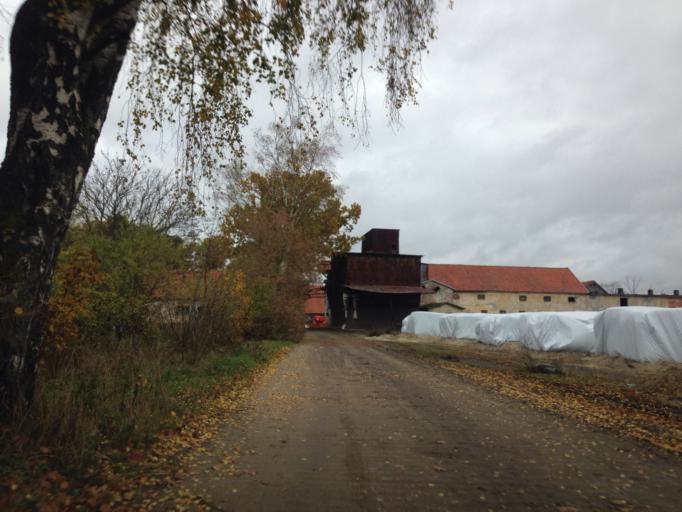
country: PL
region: Pomeranian Voivodeship
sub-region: Powiat kwidzynski
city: Prabuty
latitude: 53.7326
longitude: 19.2099
